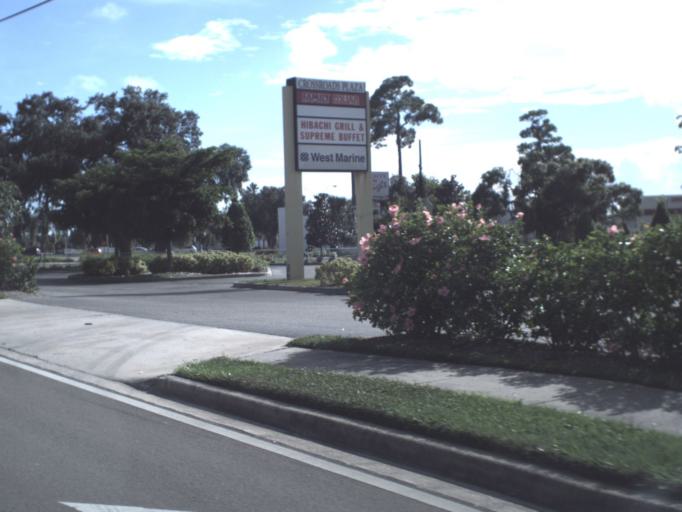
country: US
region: Florida
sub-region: Manatee County
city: West Samoset
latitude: 27.4677
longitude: -82.5630
